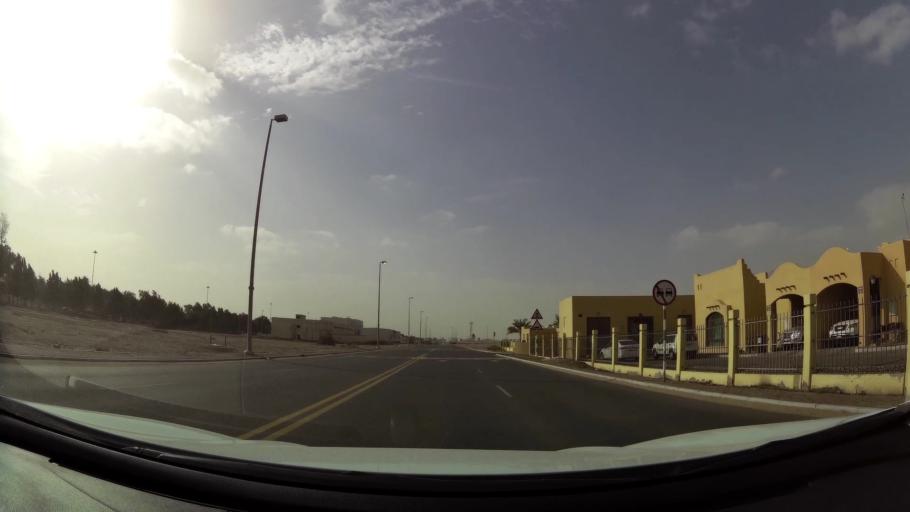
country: AE
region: Abu Dhabi
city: Abu Dhabi
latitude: 24.4085
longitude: 54.5214
